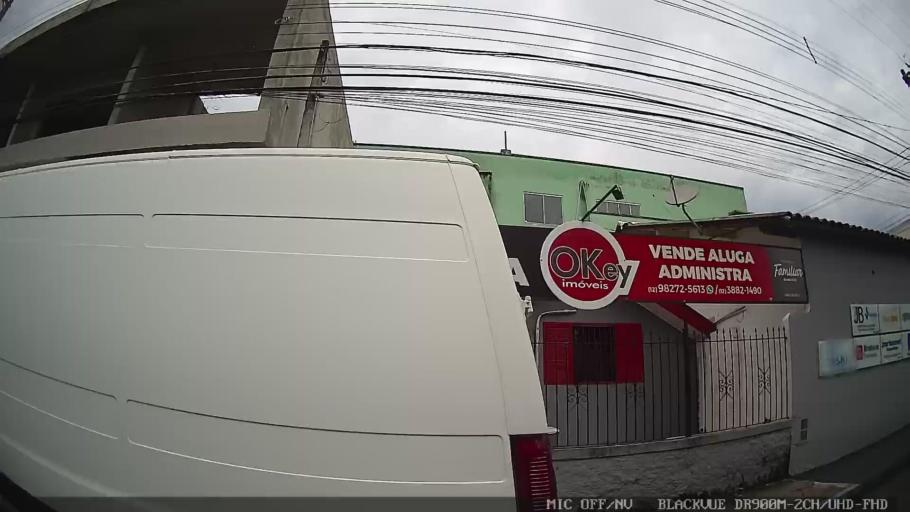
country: BR
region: Sao Paulo
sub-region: Caraguatatuba
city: Caraguatatuba
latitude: -23.6206
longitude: -45.4109
